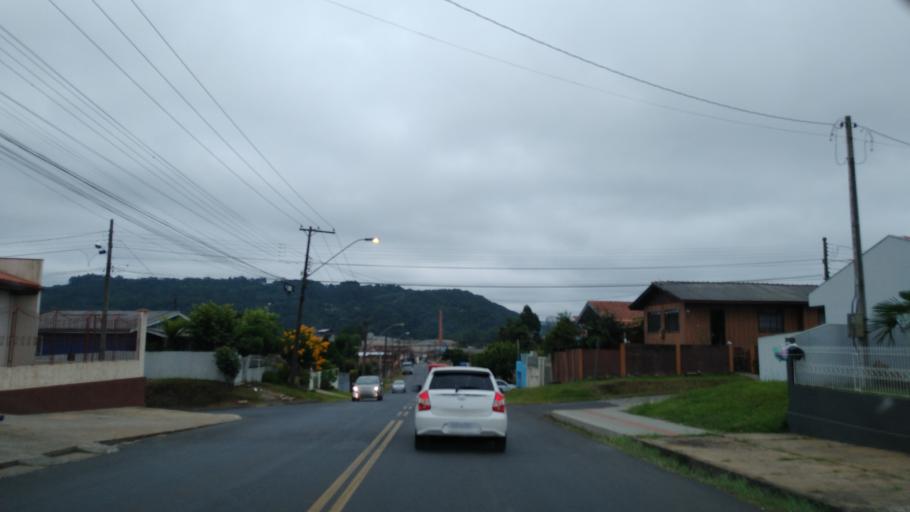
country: BR
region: Santa Catarina
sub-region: Porto Uniao
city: Porto Uniao
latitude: -26.2539
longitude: -51.0914
